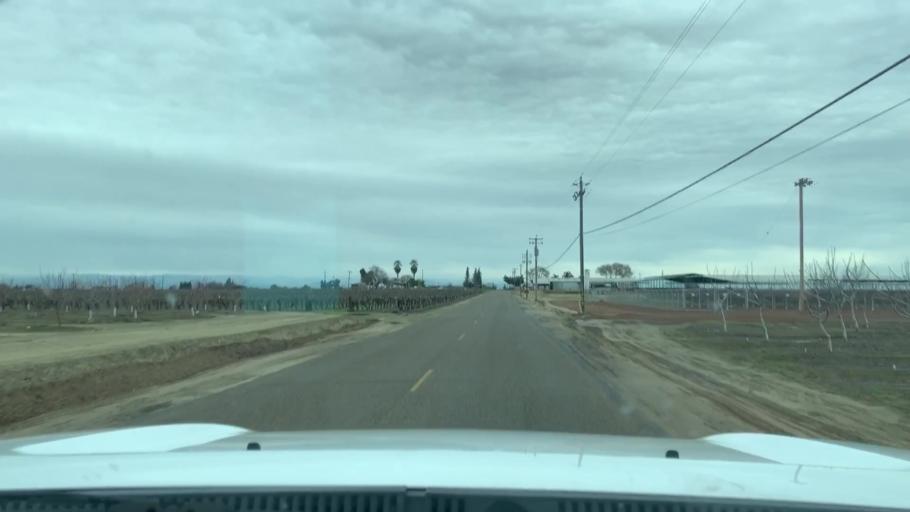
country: US
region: California
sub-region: Fresno County
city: Fowler
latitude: 36.5472
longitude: -119.7058
